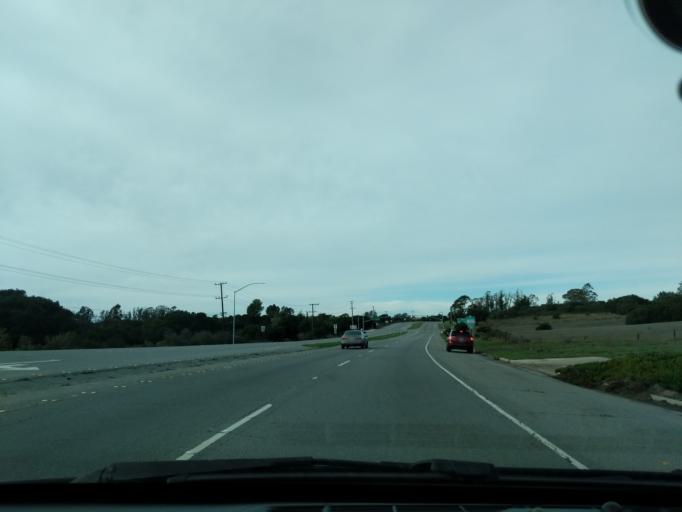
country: US
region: California
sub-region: Santa Barbara County
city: Mission Hills
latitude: 34.6789
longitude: -120.4563
